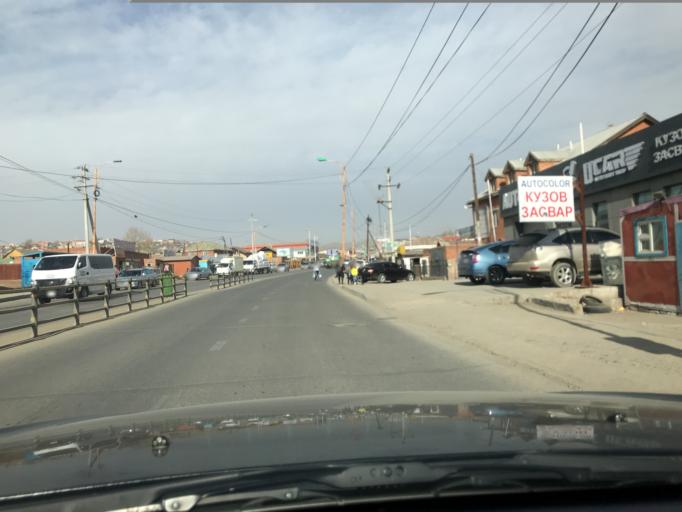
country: MN
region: Ulaanbaatar
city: Ulaanbaatar
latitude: 47.9305
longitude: 106.8885
